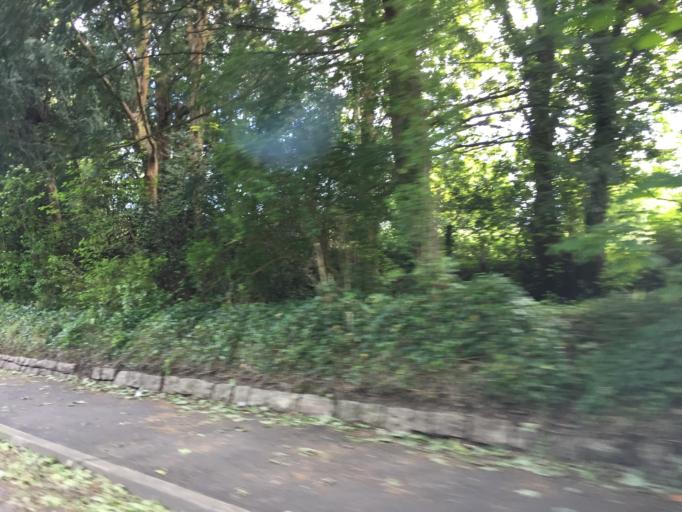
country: GB
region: Wales
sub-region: Cardiff
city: Radyr
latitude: 51.5302
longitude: -3.2470
